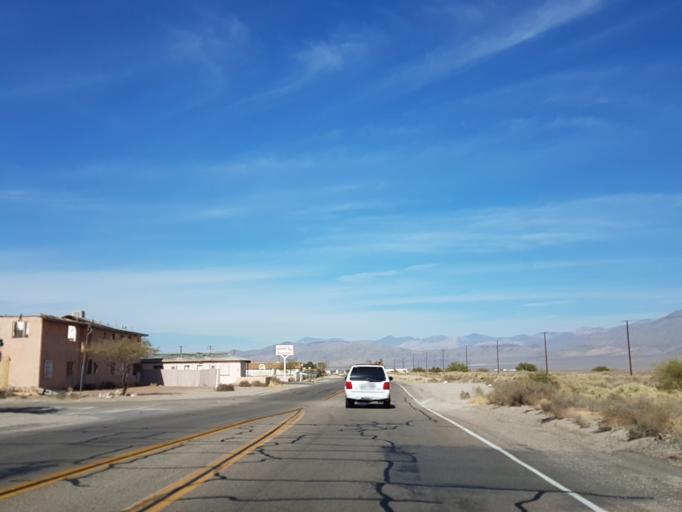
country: US
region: California
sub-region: San Bernardino County
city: Searles Valley
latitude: 35.7849
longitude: -117.3630
